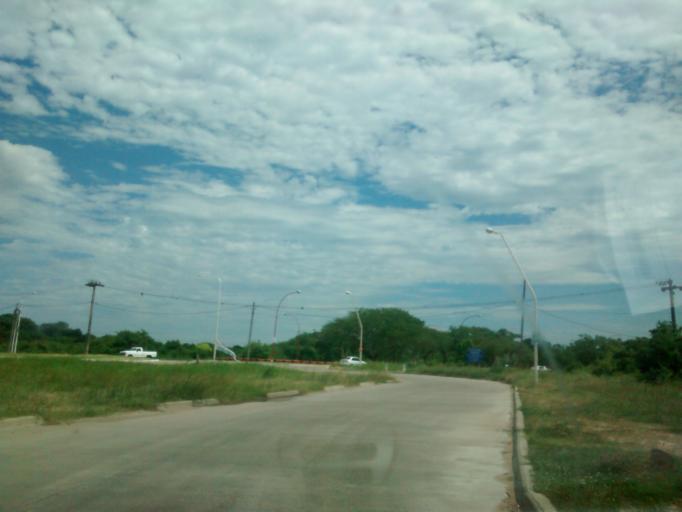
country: AR
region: Chaco
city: Resistencia
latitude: -27.4220
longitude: -58.9579
